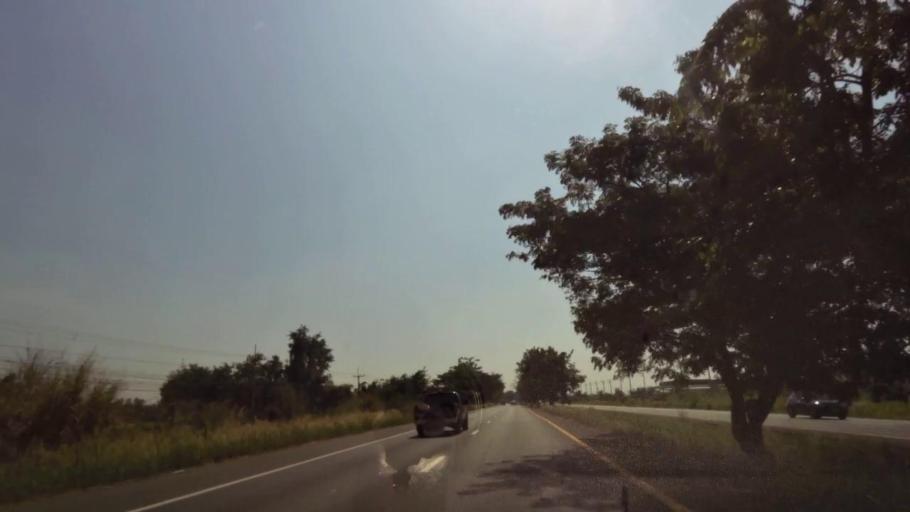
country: TH
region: Nakhon Sawan
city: Kao Liao
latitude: 15.9341
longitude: 100.1128
